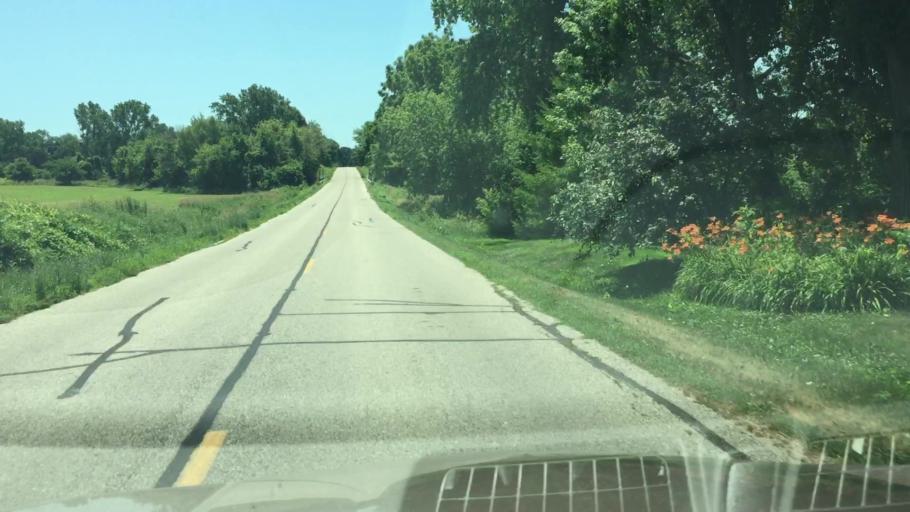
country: US
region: Wisconsin
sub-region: Fond du Lac County
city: Saint Peter
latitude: 43.9418
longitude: -88.3113
